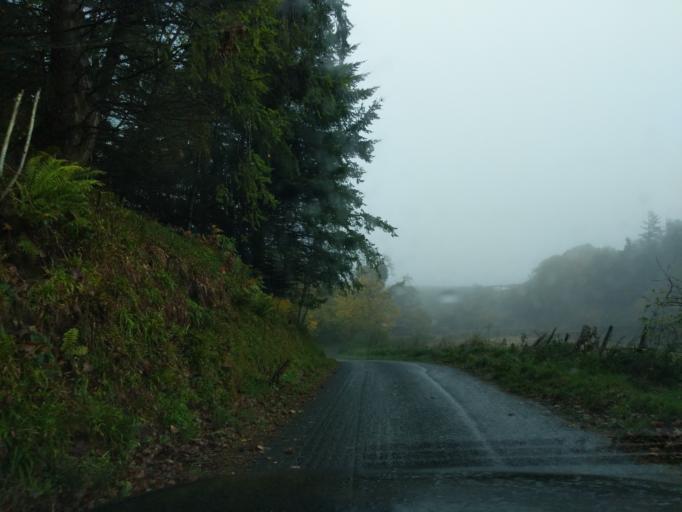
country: GB
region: Scotland
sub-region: East Lothian
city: Dunbar
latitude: 55.9432
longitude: -2.4240
